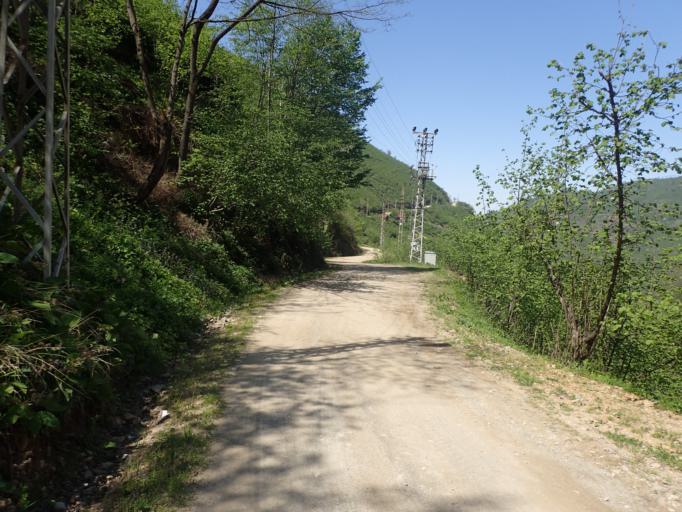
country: TR
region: Ordu
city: Kabaduz
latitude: 40.7389
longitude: 37.8931
